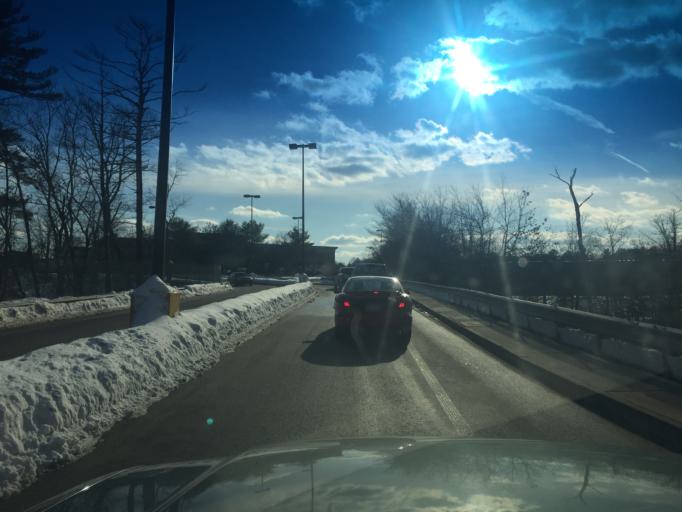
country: US
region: Massachusetts
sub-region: Norfolk County
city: Bellingham
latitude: 42.1139
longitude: -71.4616
